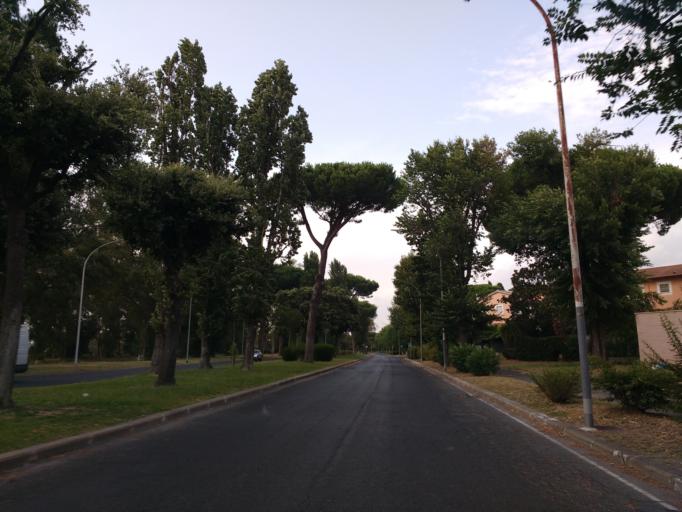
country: IT
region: Latium
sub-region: Citta metropolitana di Roma Capitale
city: Acilia-Castel Fusano-Ostia Antica
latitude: 41.7539
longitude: 12.3506
